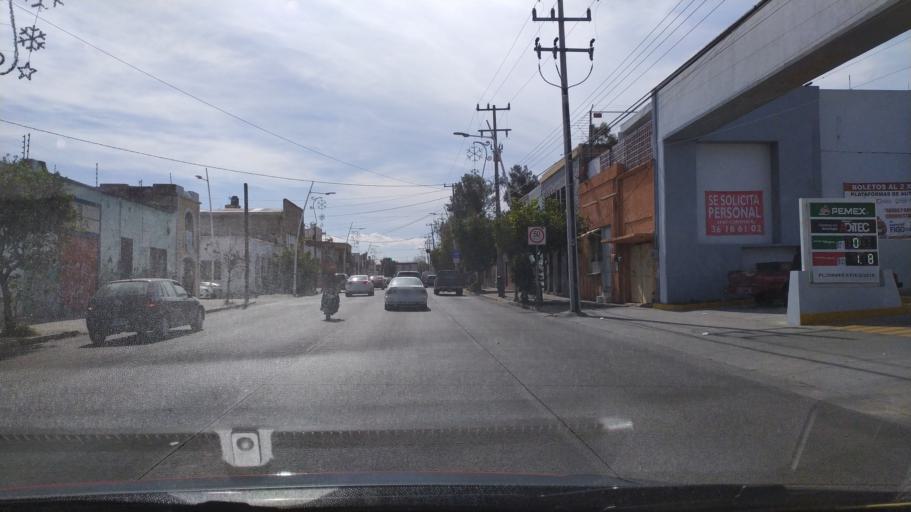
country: MX
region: Jalisco
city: Tlaquepaque
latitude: 20.6705
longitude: -103.3312
